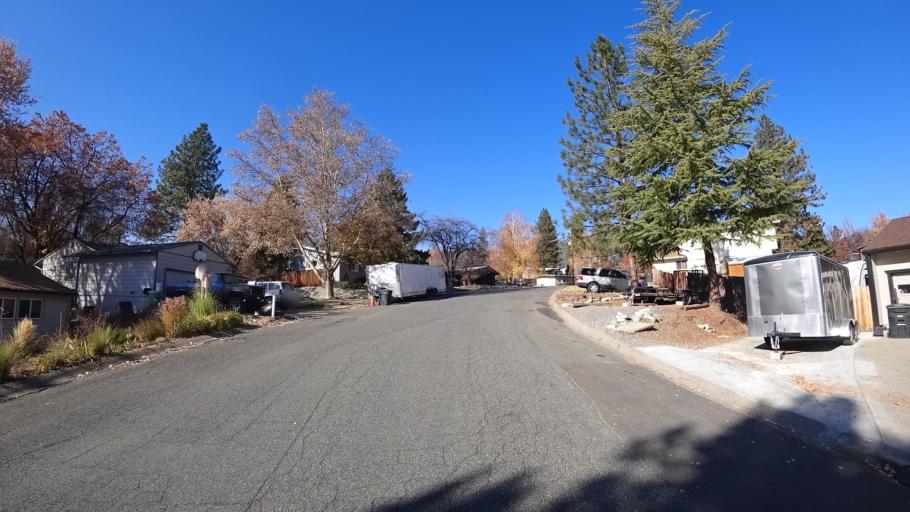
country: US
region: California
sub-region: Siskiyou County
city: Yreka
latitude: 41.7381
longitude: -122.6474
